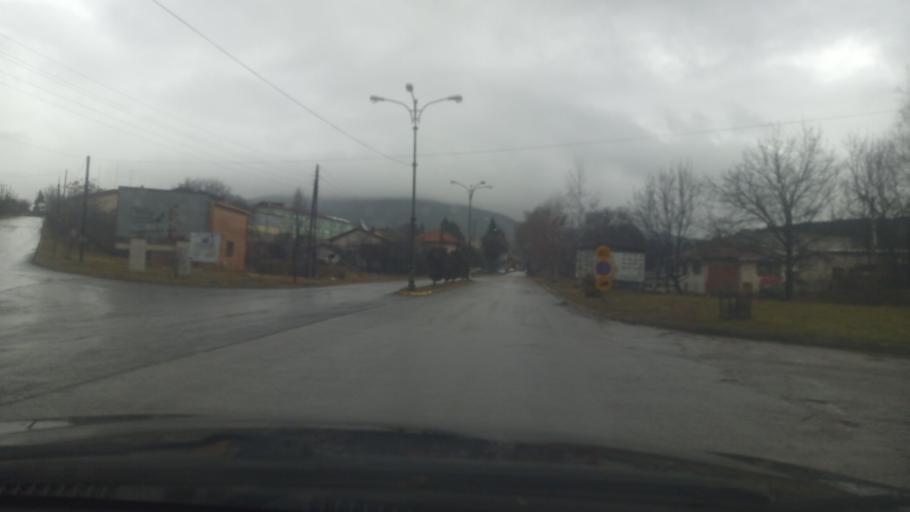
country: MK
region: Pehcevo
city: Pehcevo
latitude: 41.7612
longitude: 22.8802
